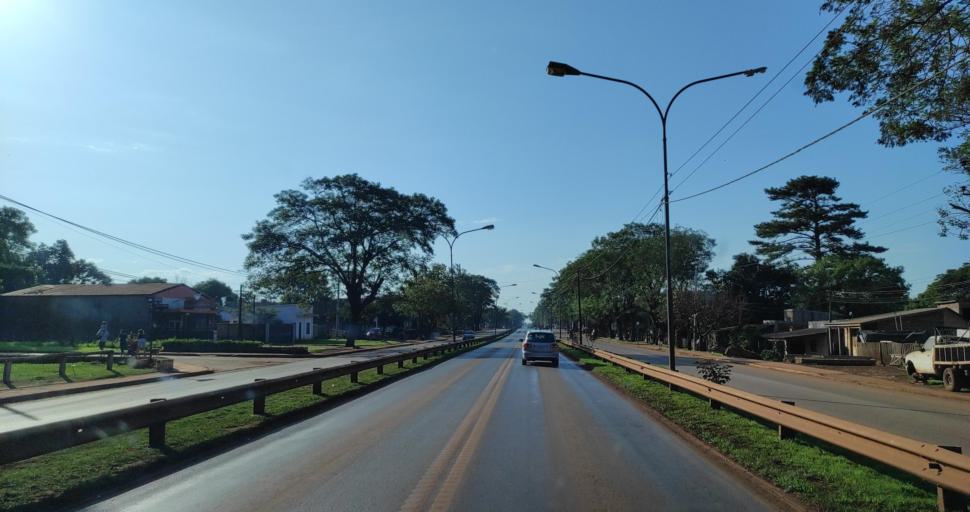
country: AR
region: Corrientes
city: Gobernador Ingeniero Valentin Virasoro
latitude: -28.0459
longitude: -56.0128
